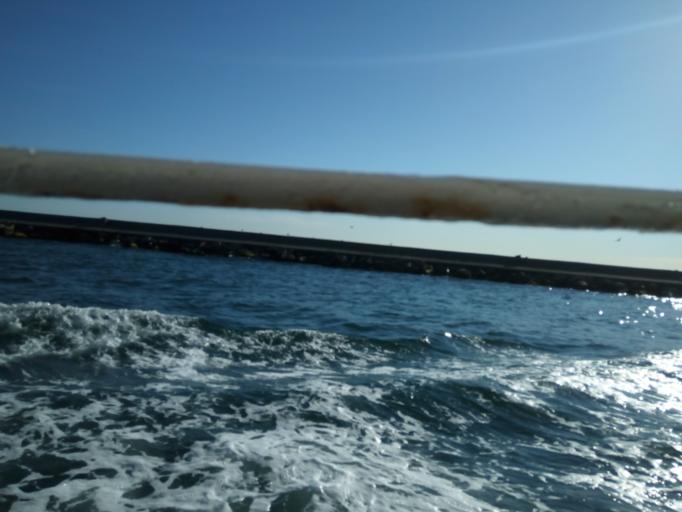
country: TR
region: Istanbul
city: UEskuedar
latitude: 41.0033
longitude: 29.0069
